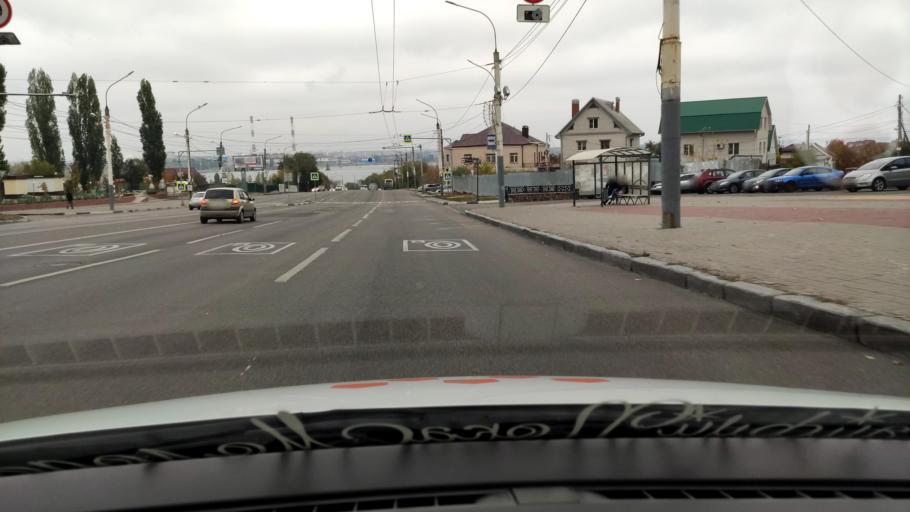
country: RU
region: Voronezj
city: Voronezh
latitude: 51.6411
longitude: 39.2037
